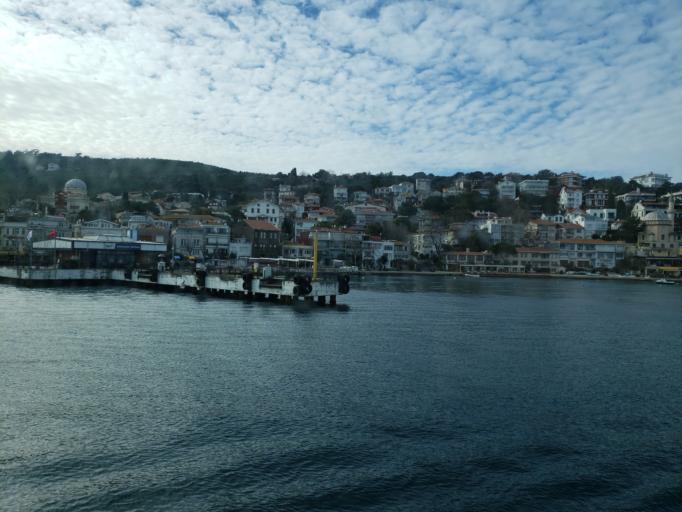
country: TR
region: Istanbul
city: Adalan
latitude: 40.8817
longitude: 29.0708
